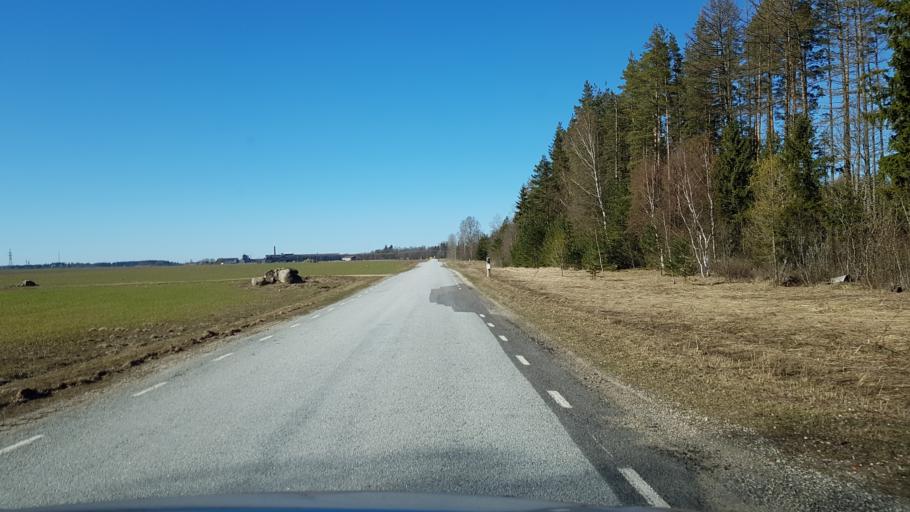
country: EE
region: Laeaene-Virumaa
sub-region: Viru-Nigula vald
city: Kunda
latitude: 59.3816
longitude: 26.5755
